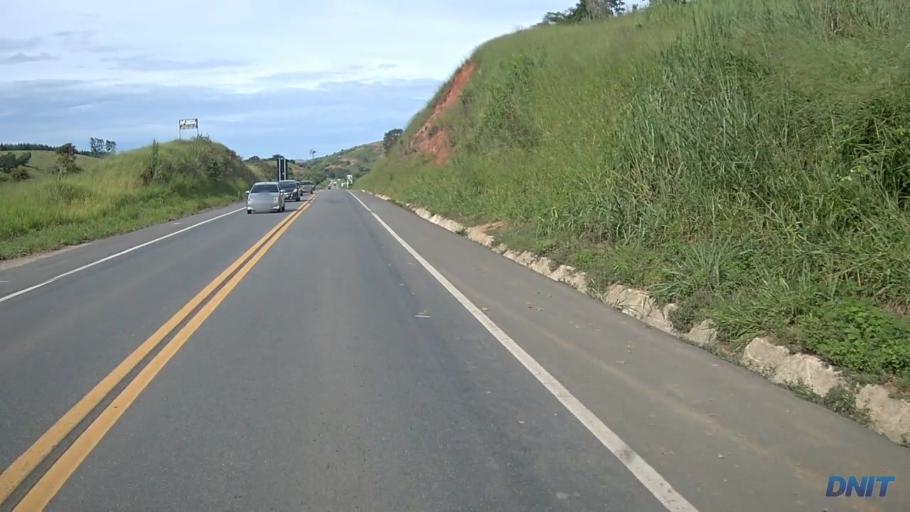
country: BR
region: Minas Gerais
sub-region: Belo Oriente
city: Belo Oriente
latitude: -19.2089
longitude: -42.3026
